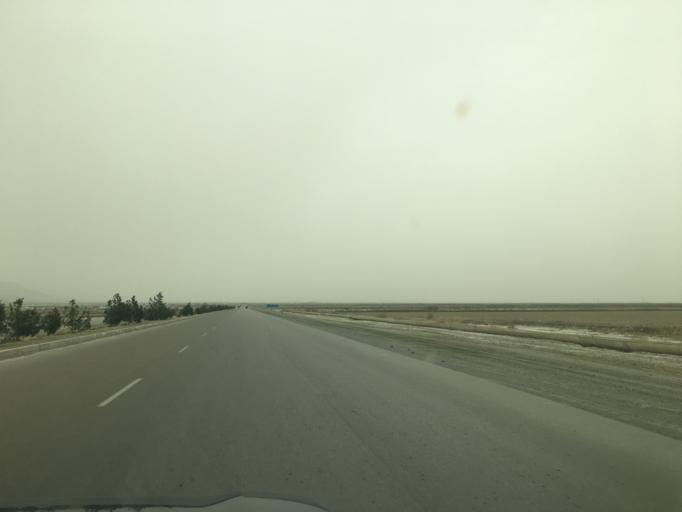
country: TM
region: Ahal
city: Baharly
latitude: 38.3718
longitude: 57.5156
